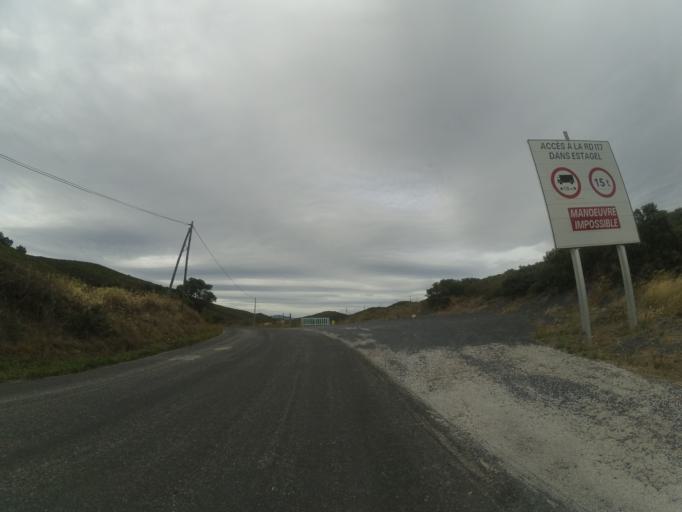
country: FR
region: Languedoc-Roussillon
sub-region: Departement des Pyrenees-Orientales
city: Corneilla-la-Riviere
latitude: 42.7277
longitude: 2.7407
